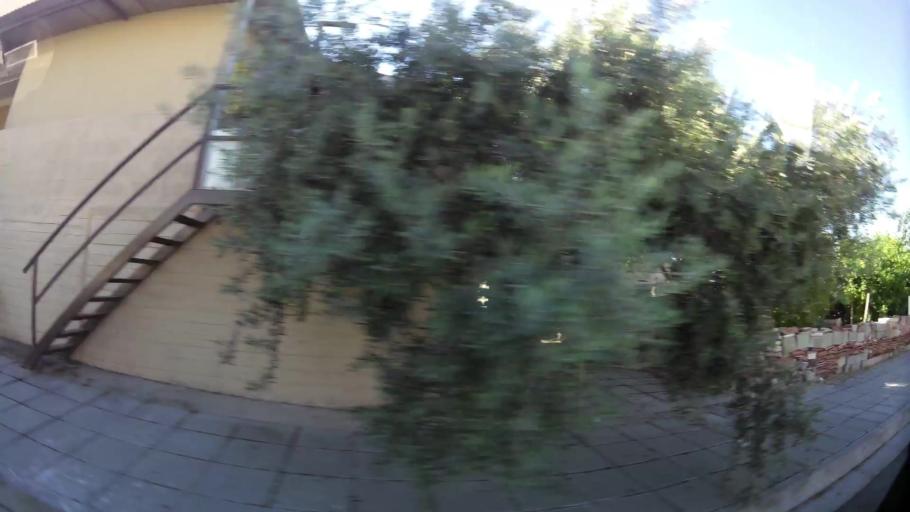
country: CY
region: Larnaka
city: Larnaca
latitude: 34.9360
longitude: 33.6105
